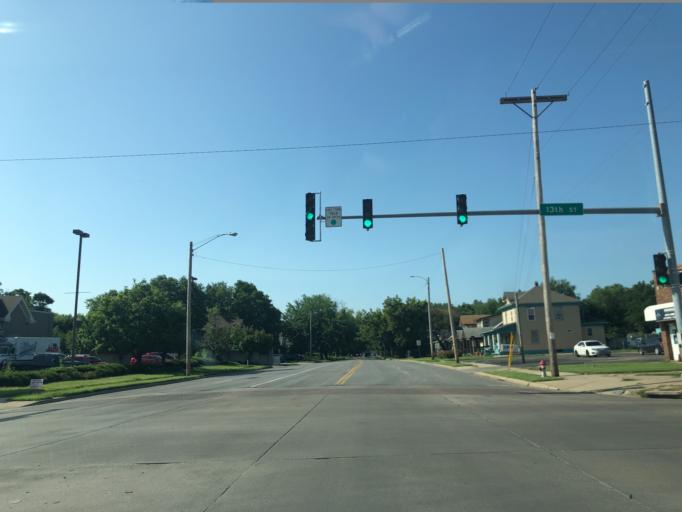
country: US
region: Kansas
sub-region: Sedgwick County
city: Wichita
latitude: 37.7084
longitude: -97.3420
